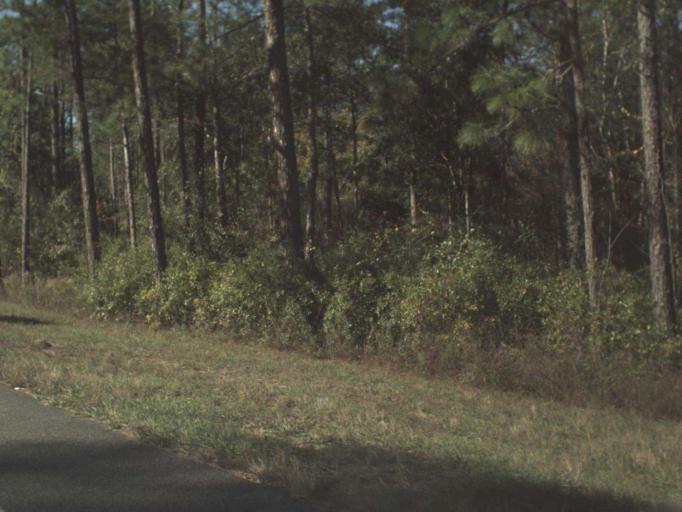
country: US
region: Florida
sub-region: Okaloosa County
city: Crestview
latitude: 30.8502
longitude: -86.7708
